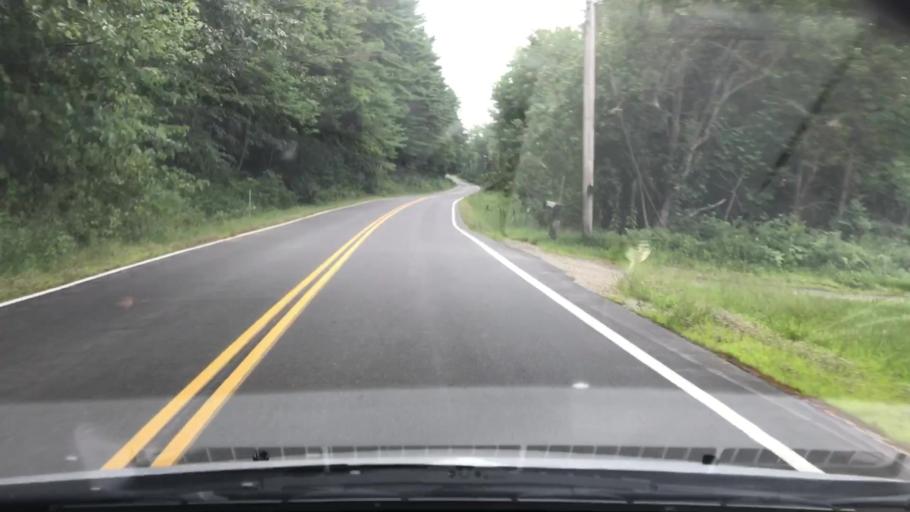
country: US
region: New Hampshire
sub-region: Grafton County
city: Woodsville
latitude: 44.2196
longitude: -72.0488
